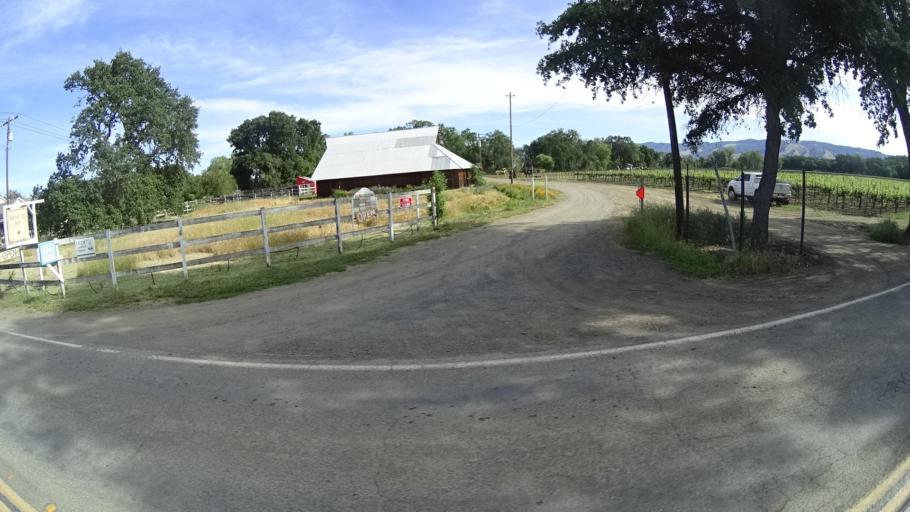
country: US
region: California
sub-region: Lake County
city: Kelseyville
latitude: 39.0112
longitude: -122.8276
